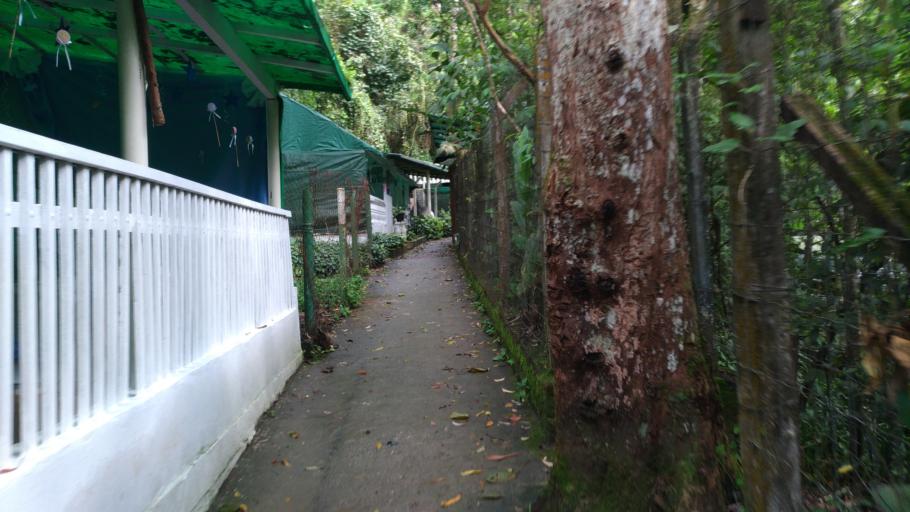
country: BR
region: Sao Paulo
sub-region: Sao Bernardo Do Campo
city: Sao Bernardo do Campo
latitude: -23.7454
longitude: -46.5149
